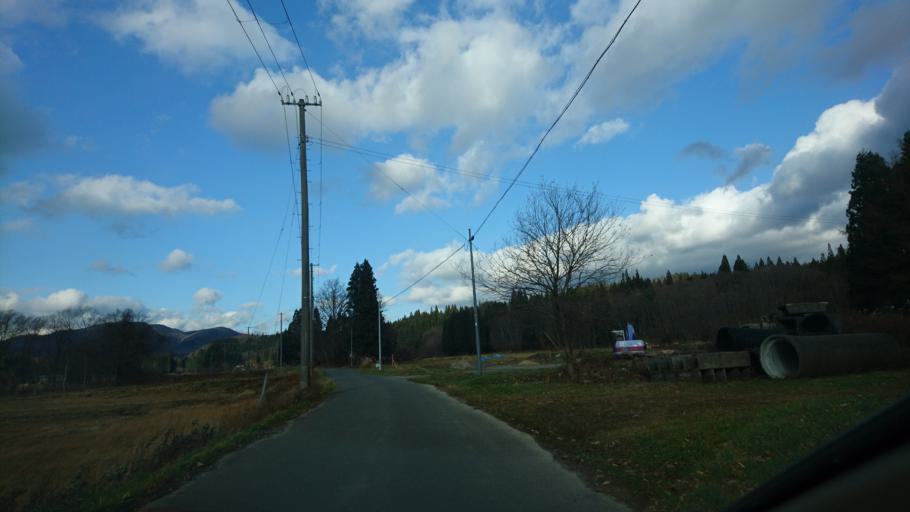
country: JP
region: Akita
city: Kakunodatemachi
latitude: 39.4574
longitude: 140.7861
